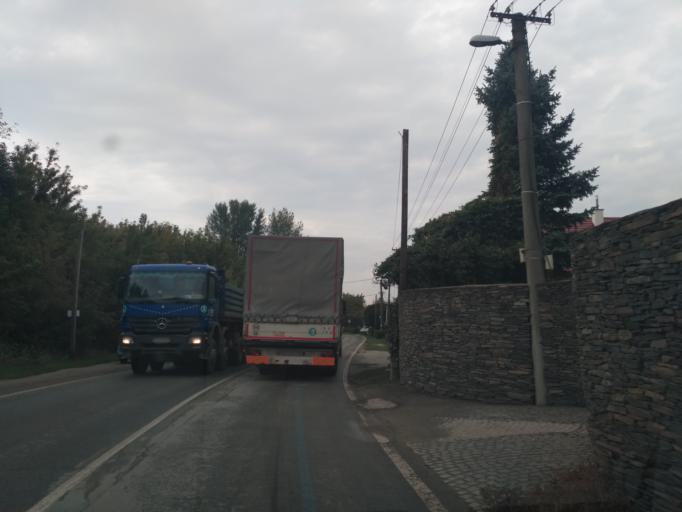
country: SK
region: Kosicky
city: Kosice
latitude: 48.7458
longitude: 21.2487
